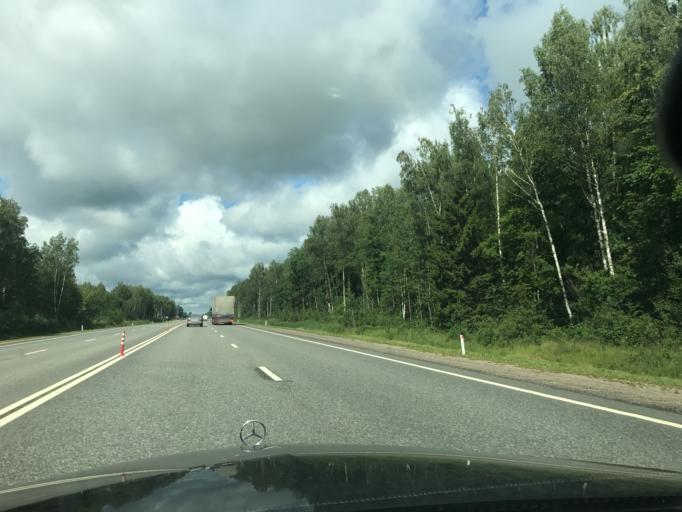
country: RU
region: Smolensk
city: Golynki
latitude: 54.7453
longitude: 31.4378
